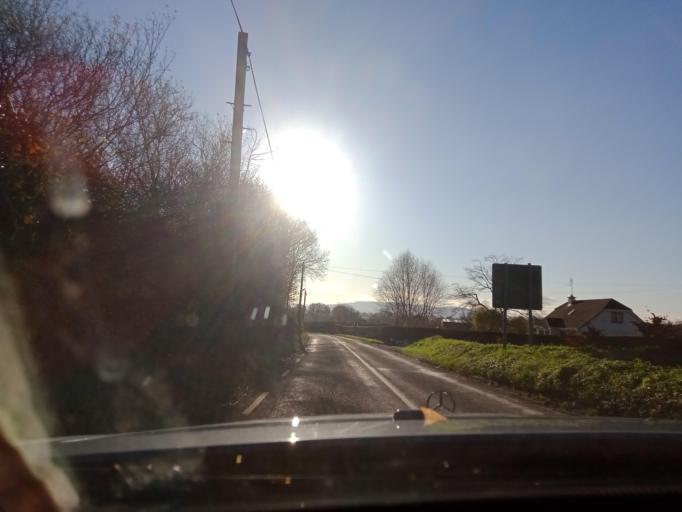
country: IE
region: Leinster
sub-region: Kilkenny
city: Piltown
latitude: 52.3918
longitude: -7.3489
